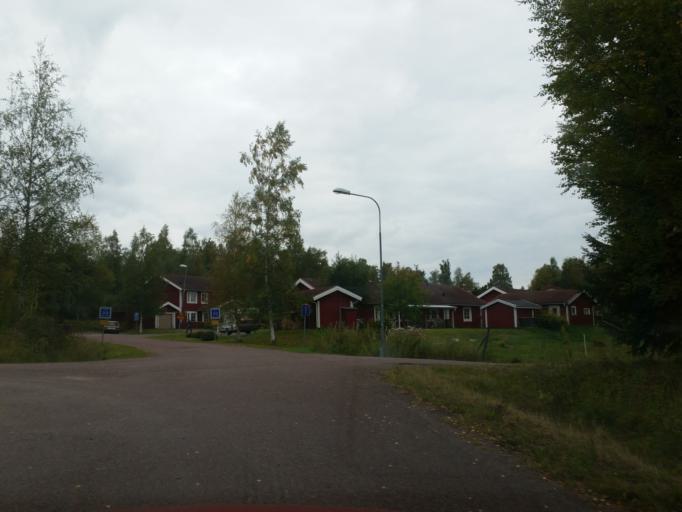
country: SE
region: Dalarna
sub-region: Leksand Municipality
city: Smedby
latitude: 60.6750
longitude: 15.1295
